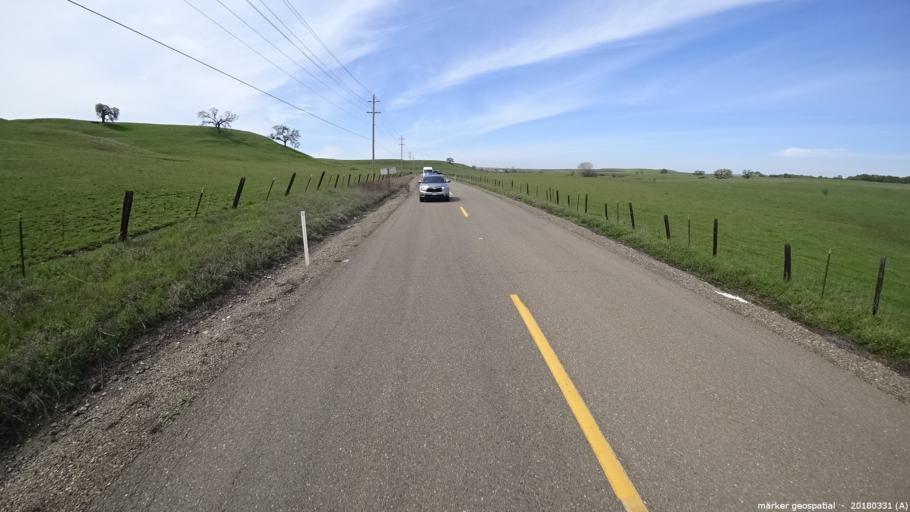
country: US
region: California
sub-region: Sacramento County
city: Rancho Murieta
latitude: 38.5174
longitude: -121.1069
